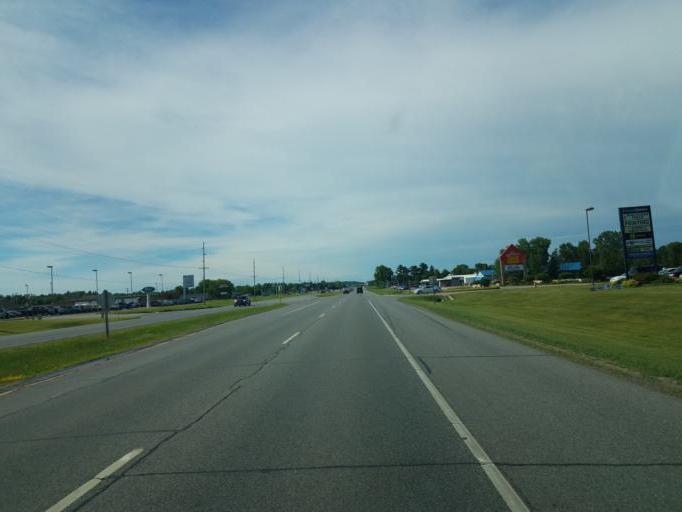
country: US
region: Wisconsin
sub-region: Monroe County
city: Tomah
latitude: 44.0027
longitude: -90.5048
